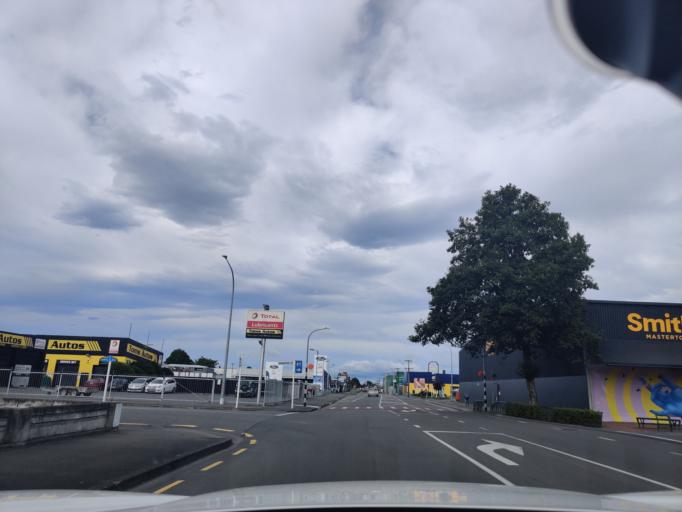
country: NZ
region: Wellington
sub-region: Masterton District
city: Masterton
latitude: -40.9511
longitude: 175.6618
